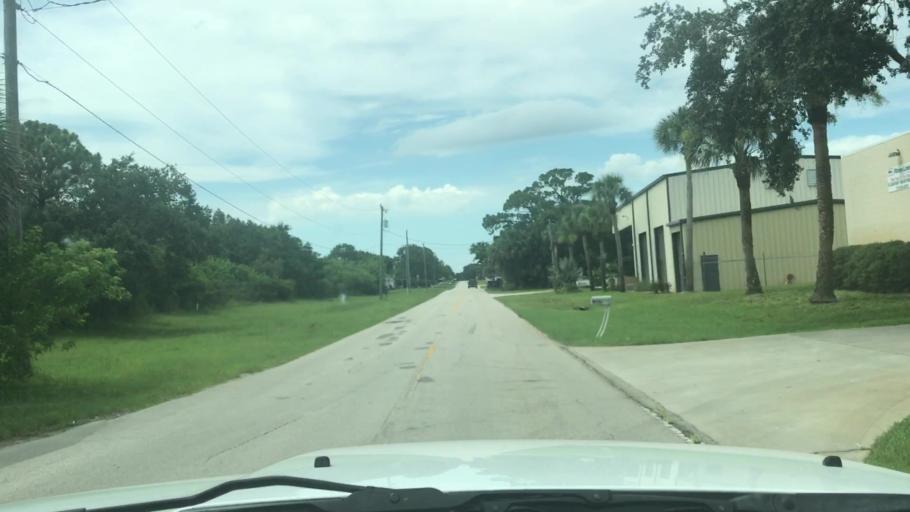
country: US
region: Florida
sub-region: Indian River County
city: Florida Ridge
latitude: 27.5615
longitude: -80.3702
